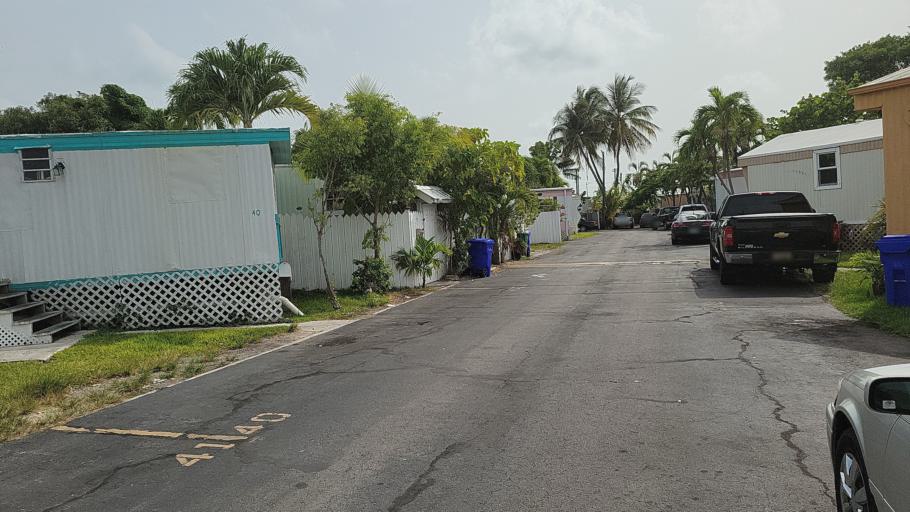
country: US
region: Florida
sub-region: Monroe County
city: Key West
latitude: 24.5663
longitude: -81.7628
